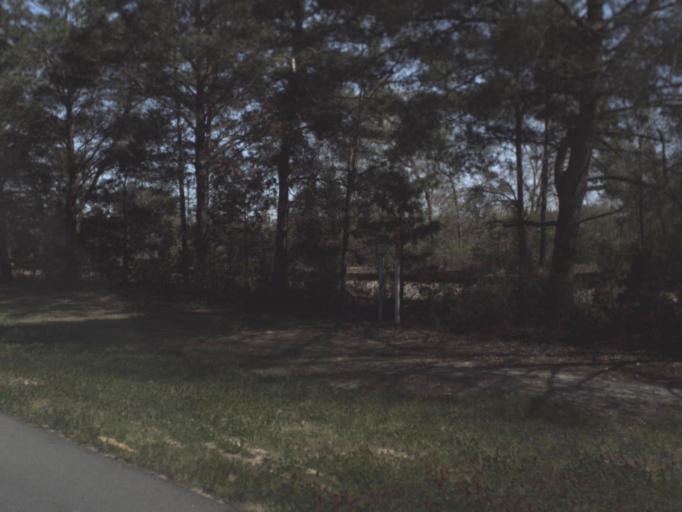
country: US
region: Florida
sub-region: Walton County
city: DeFuniak Springs
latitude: 30.7465
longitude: -86.2290
